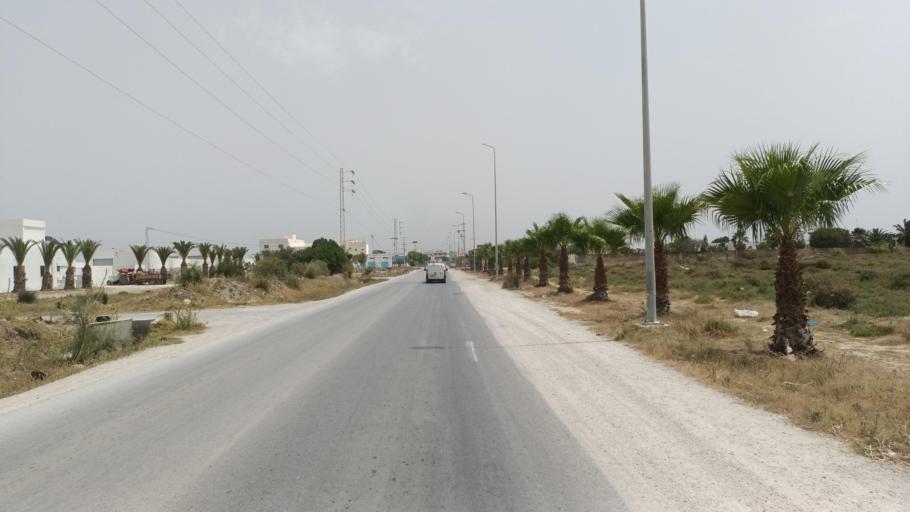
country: TN
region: Nabul
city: Manzil Bu Zalafah
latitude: 36.7118
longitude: 10.4815
